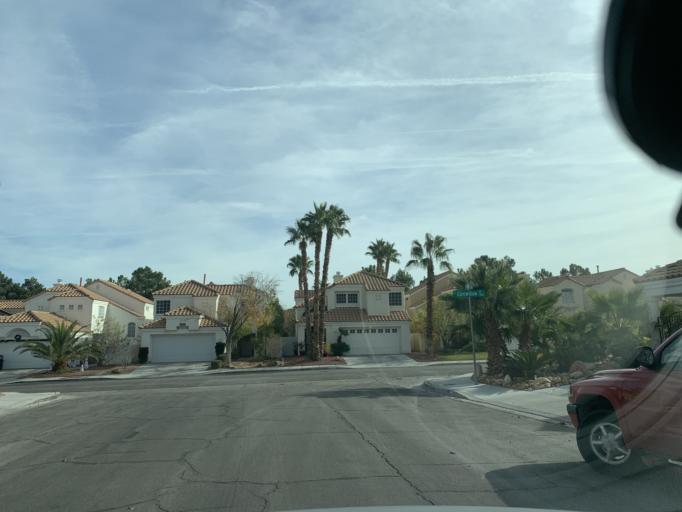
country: US
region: Nevada
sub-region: Clark County
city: Summerlin South
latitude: 36.1505
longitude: -115.2970
